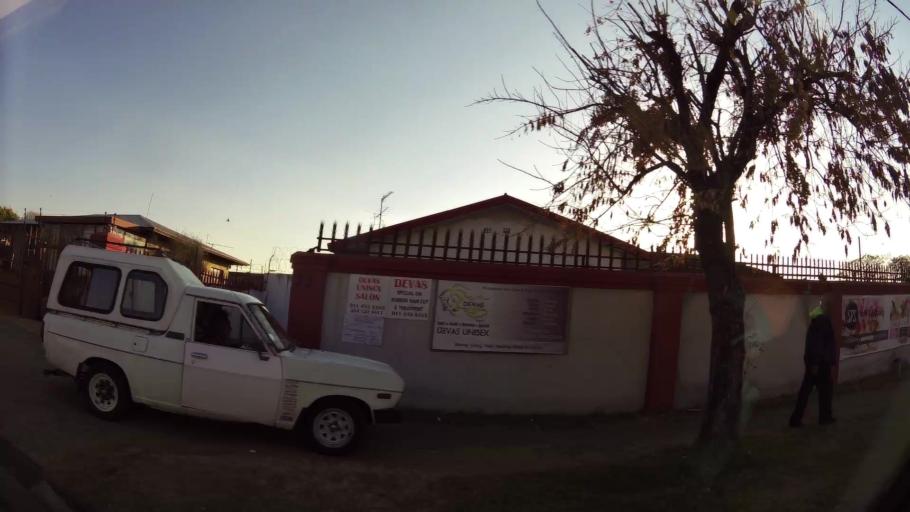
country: ZA
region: Gauteng
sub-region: City of Johannesburg Metropolitan Municipality
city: Johannesburg
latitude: -26.2488
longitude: 28.0070
